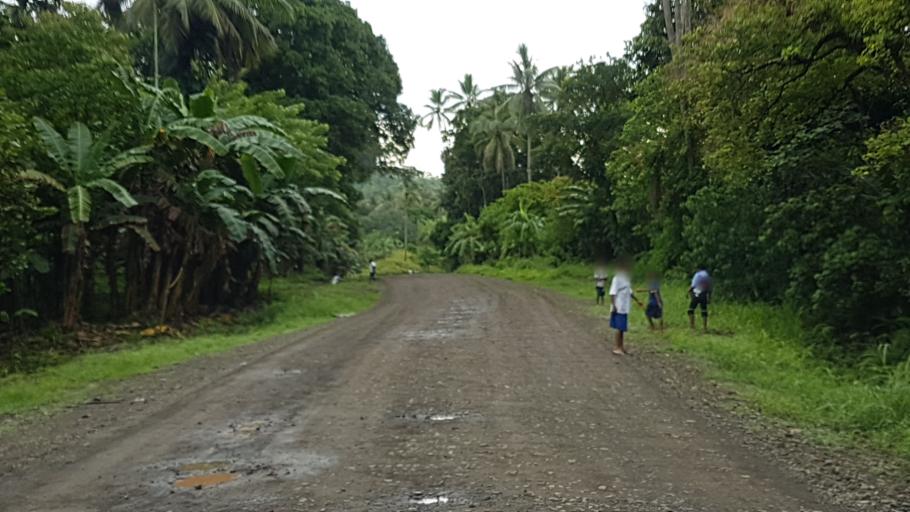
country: PG
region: Milne Bay
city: Alotau
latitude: -10.3192
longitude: 150.6764
